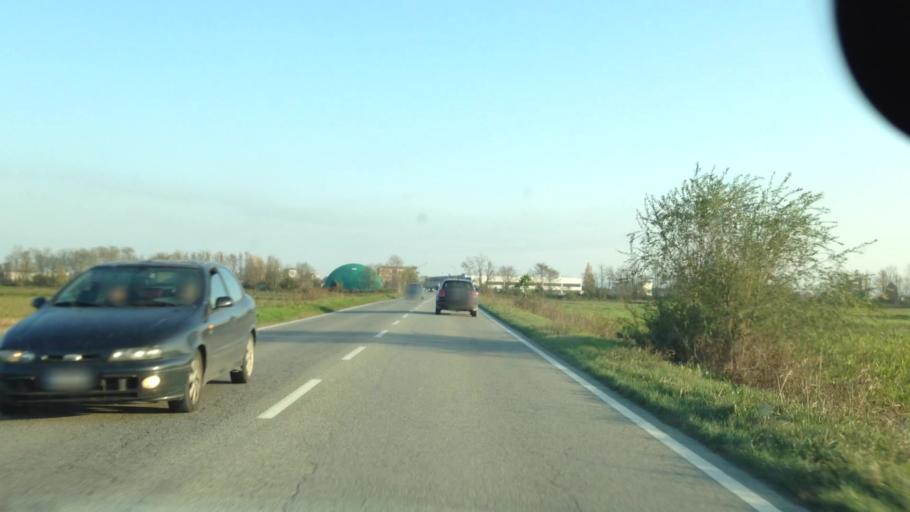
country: IT
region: Piedmont
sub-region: Provincia di Vercelli
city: Livorno Ferraris
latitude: 45.2894
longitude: 8.0577
